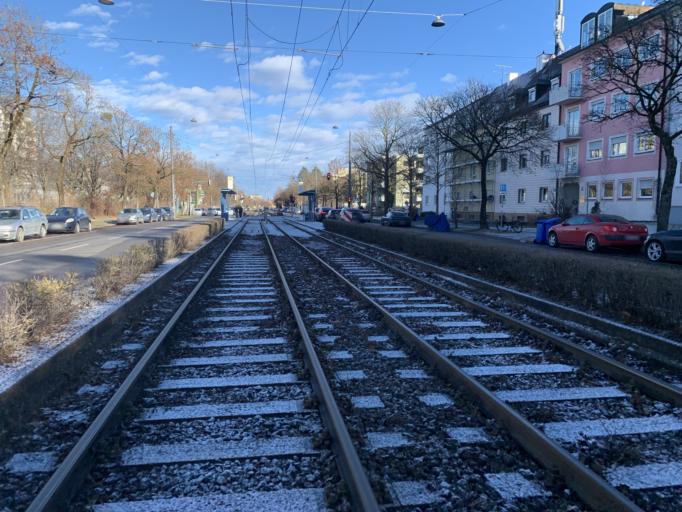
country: DE
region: Bavaria
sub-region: Upper Bavaria
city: Munich
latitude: 48.1005
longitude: 11.5664
